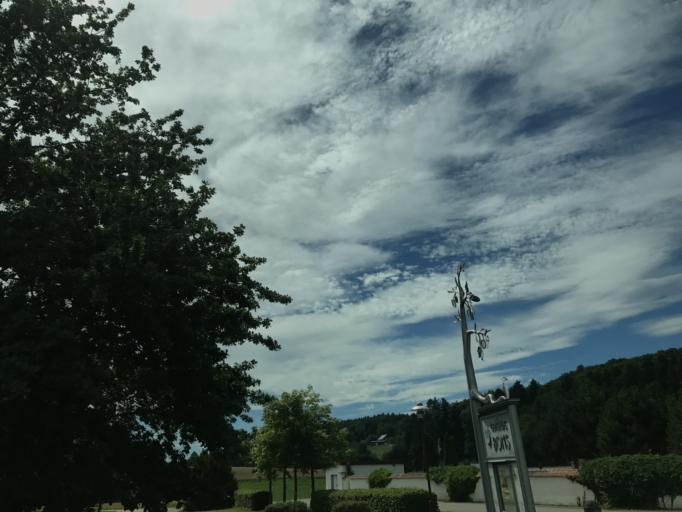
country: DE
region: Baden-Wuerttemberg
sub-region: Tuebingen Region
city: Boms
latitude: 47.9721
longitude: 9.5074
